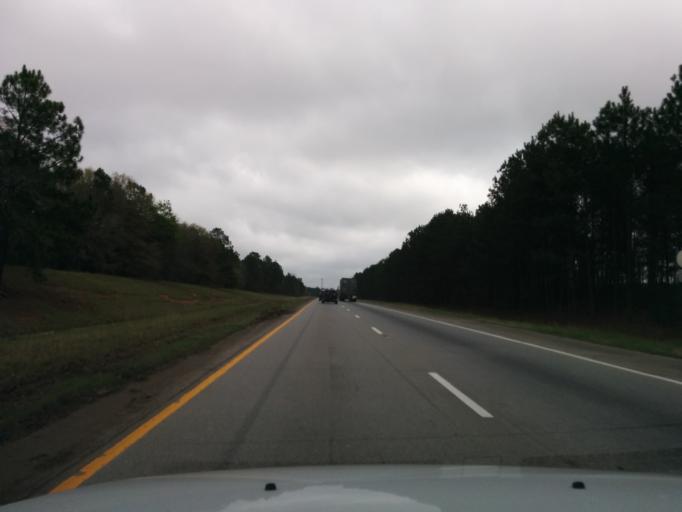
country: US
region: Georgia
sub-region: Candler County
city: Metter
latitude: 32.3823
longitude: -82.2338
